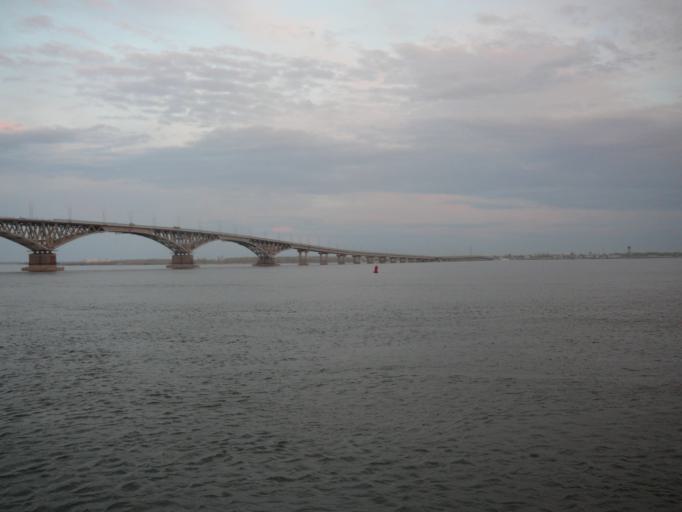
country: RU
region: Saratov
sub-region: Saratovskiy Rayon
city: Saratov
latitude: 51.5265
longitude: 46.0594
